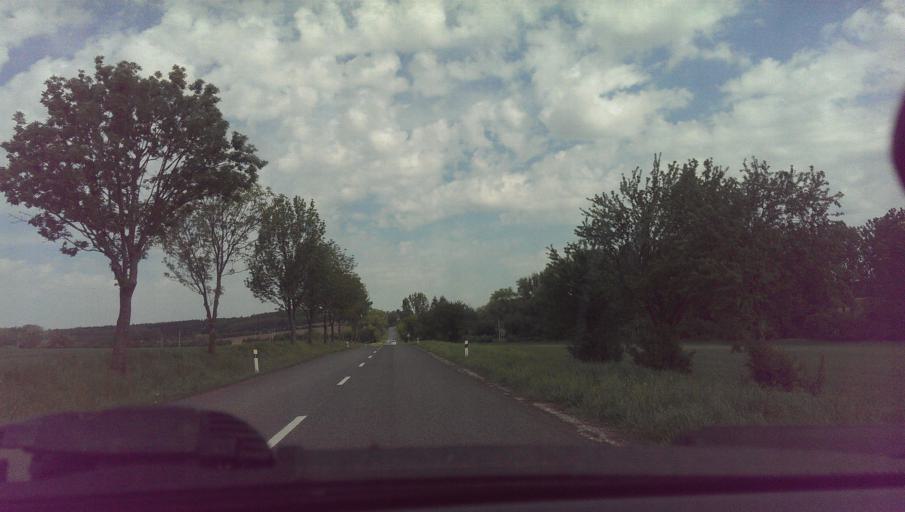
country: CZ
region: Zlin
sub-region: Okres Zlin
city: Otrokovice
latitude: 49.2279
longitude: 17.5362
